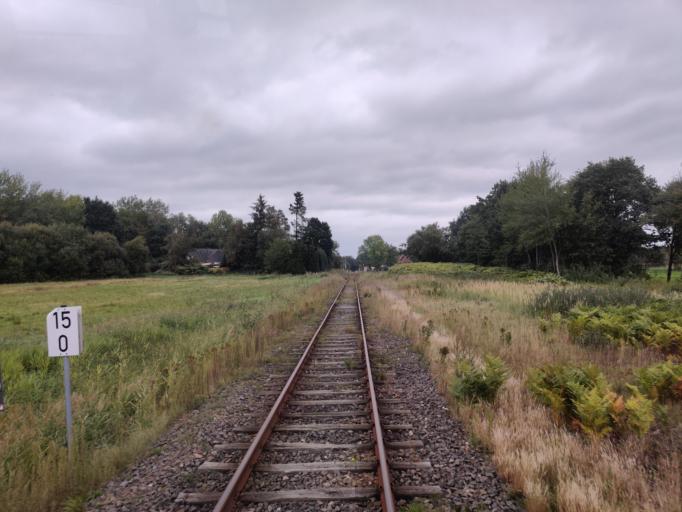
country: DE
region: Lower Saxony
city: Gnarrenburg
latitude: 53.4128
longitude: 9.0128
